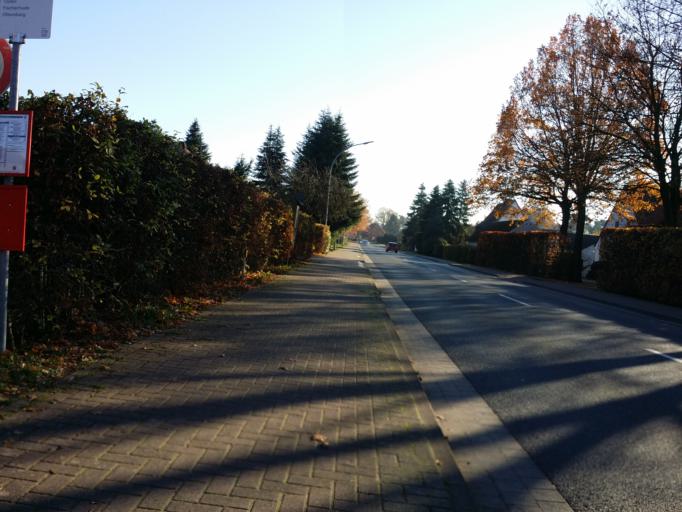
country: DE
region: Lower Saxony
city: Langwedel
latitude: 53.0335
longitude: 9.1569
